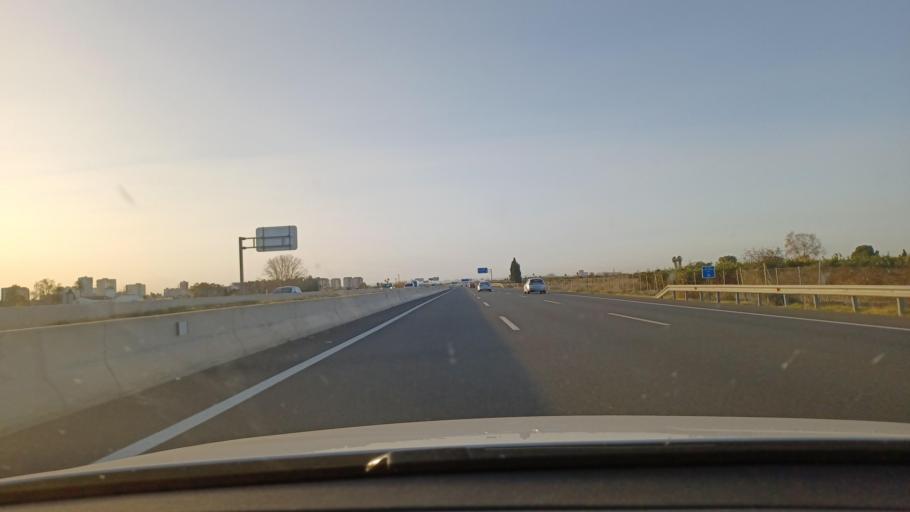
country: ES
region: Valencia
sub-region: Provincia de Valencia
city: Puig
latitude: 39.5785
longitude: -0.2948
